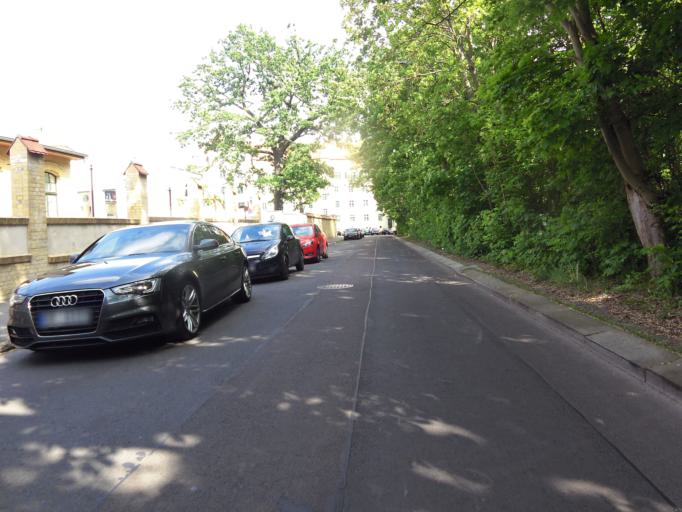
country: DE
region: Saxony
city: Leipzig
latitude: 51.3688
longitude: 12.3584
